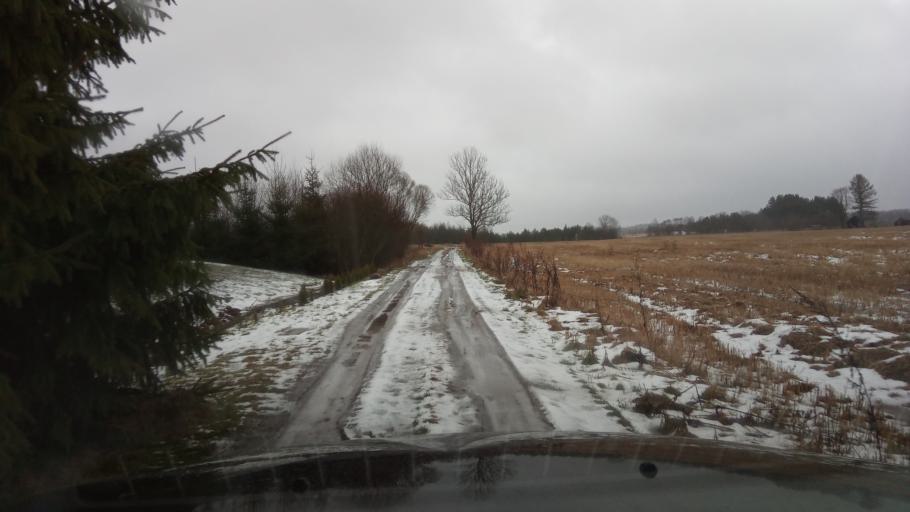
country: LT
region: Utenos apskritis
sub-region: Utena
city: Utena
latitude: 55.3707
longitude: 25.7592
